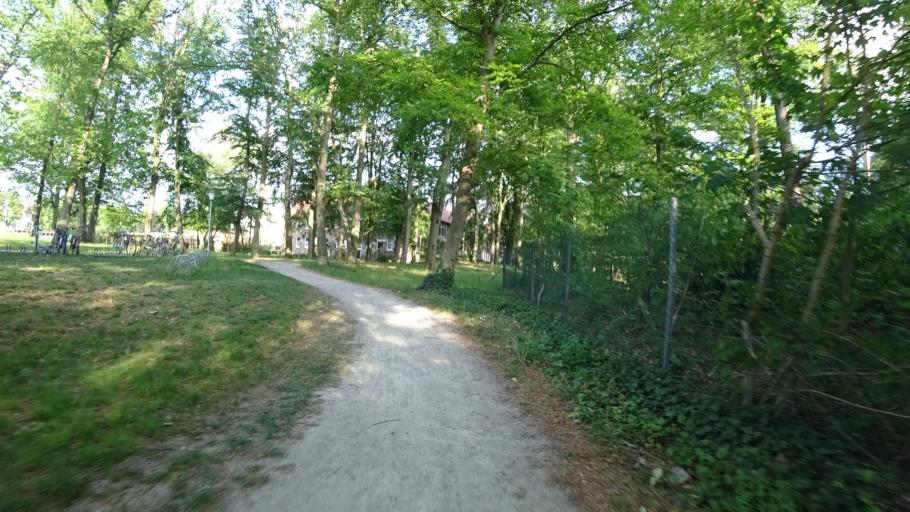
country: DE
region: North Rhine-Westphalia
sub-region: Regierungsbezirk Detmold
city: Guetersloh
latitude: 51.8945
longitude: 8.3489
